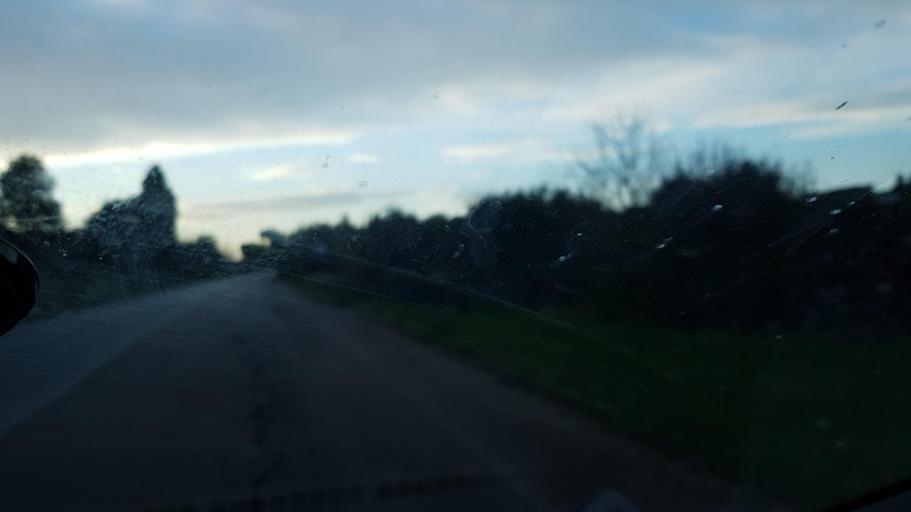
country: IT
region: Apulia
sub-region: Provincia di Brindisi
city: Ceglie Messapica
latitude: 40.6433
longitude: 17.5393
